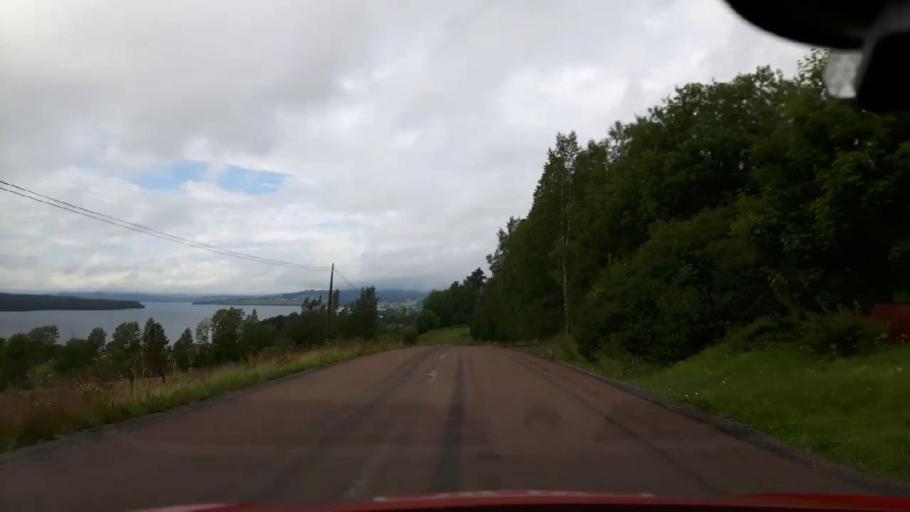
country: SE
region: Jaemtland
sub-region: Krokoms Kommun
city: Valla
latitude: 63.3651
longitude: 14.0583
